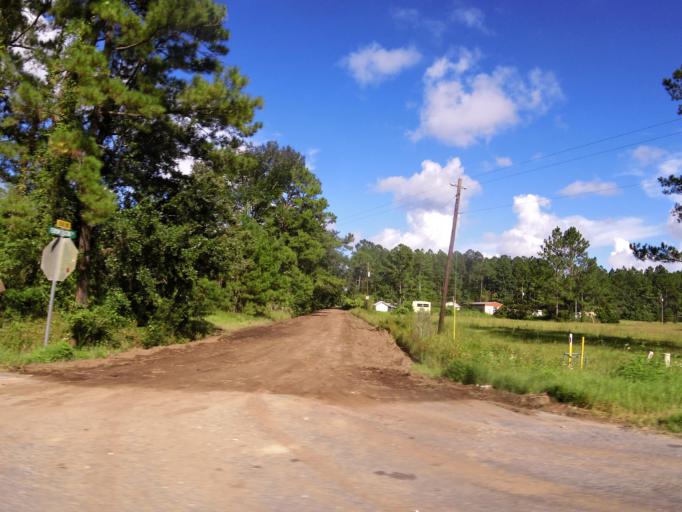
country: US
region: Georgia
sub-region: Camden County
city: Woodbine
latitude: 31.0711
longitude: -81.7277
